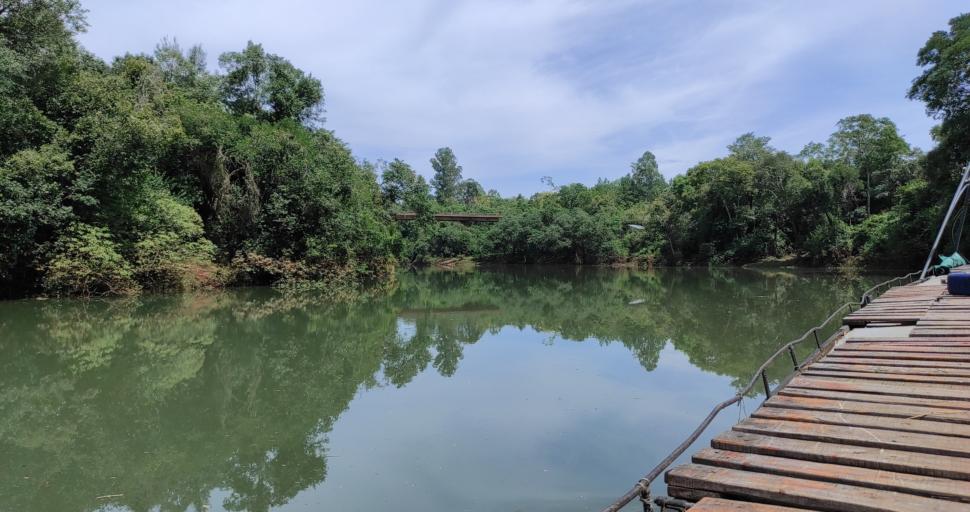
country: AR
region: Misiones
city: El Soberbio
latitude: -27.2808
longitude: -54.1941
